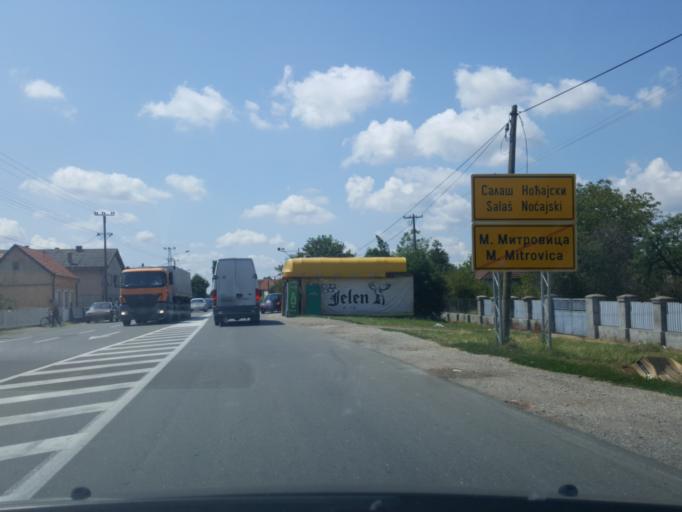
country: RS
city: Macvanska Mitrovica
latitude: 44.9564
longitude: 19.6000
